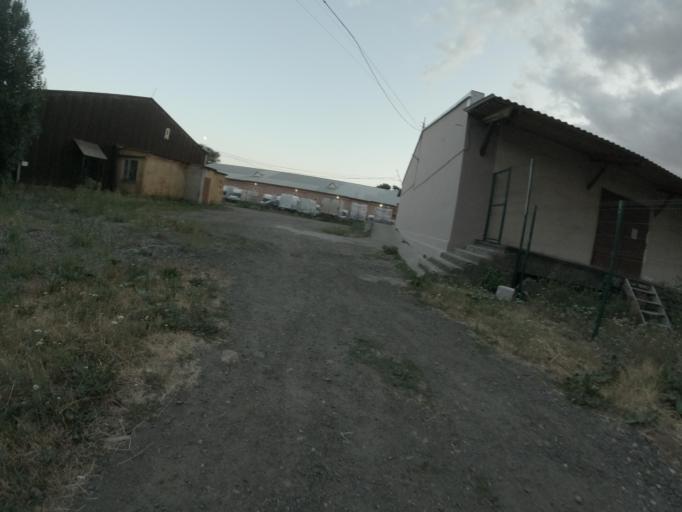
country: RU
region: St.-Petersburg
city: Saint Petersburg
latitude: 59.9007
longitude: 30.3277
